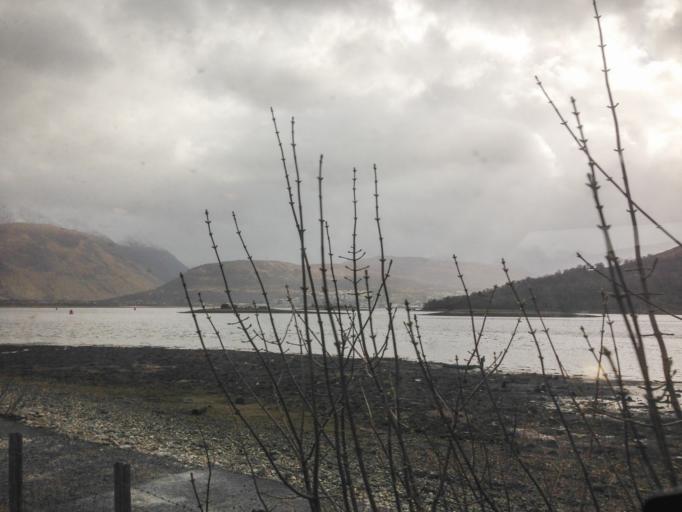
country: GB
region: Scotland
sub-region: Highland
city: Fort William
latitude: 56.8431
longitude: -5.1300
